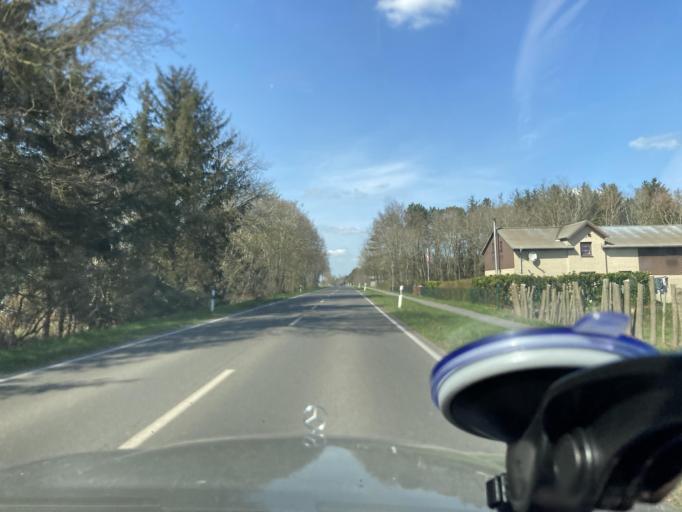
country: DE
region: Schleswig-Holstein
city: Stelle-Wittenwurth
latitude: 54.2749
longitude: 9.0471
